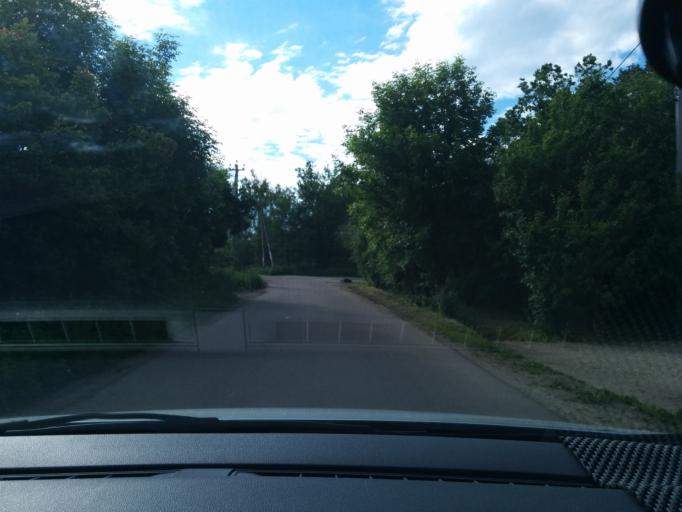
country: RU
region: Moskovskaya
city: Lugovaya
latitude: 56.0536
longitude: 37.4792
